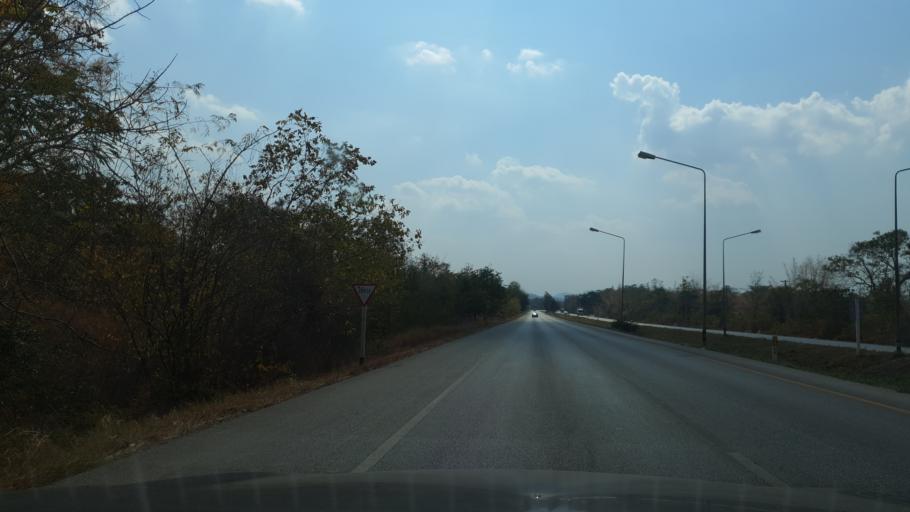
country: TH
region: Lampang
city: Mae Phrik
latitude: 17.4269
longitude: 99.1580
